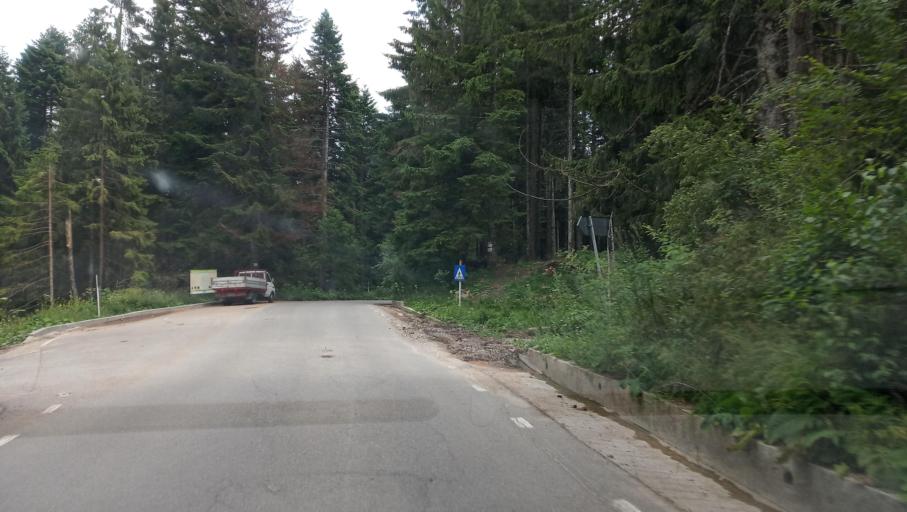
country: RO
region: Prahova
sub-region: Oras Sinaia
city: Sinaia
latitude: 45.3212
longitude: 25.5145
